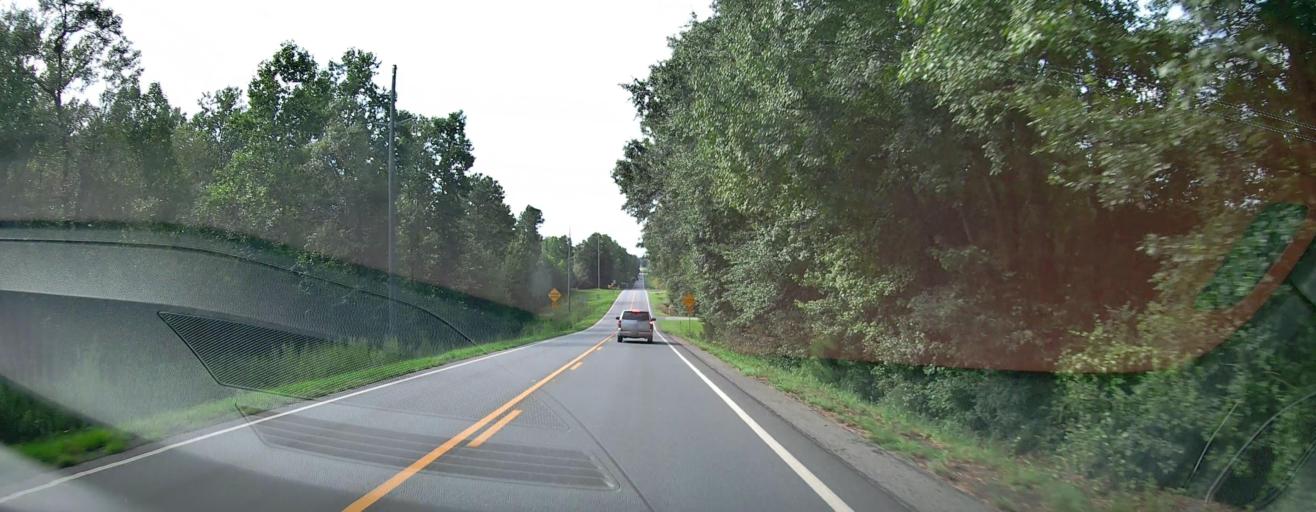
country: US
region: Georgia
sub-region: Upson County
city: Hannahs Mill
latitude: 32.9798
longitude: -84.4971
